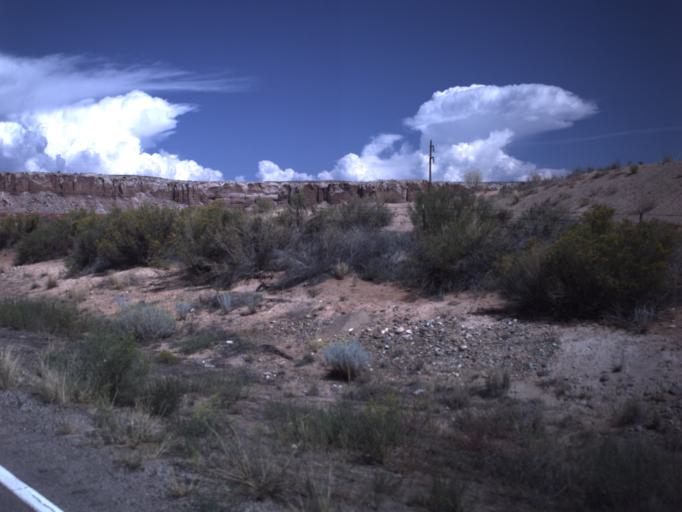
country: US
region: Utah
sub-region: San Juan County
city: Blanding
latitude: 37.2636
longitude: -109.6250
